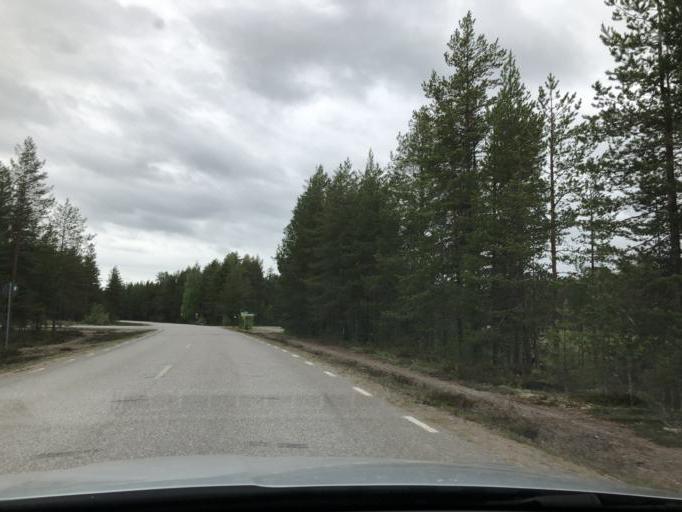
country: SE
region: Norrbotten
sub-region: Pitea Kommun
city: Pitea
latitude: 65.2389
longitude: 21.5205
